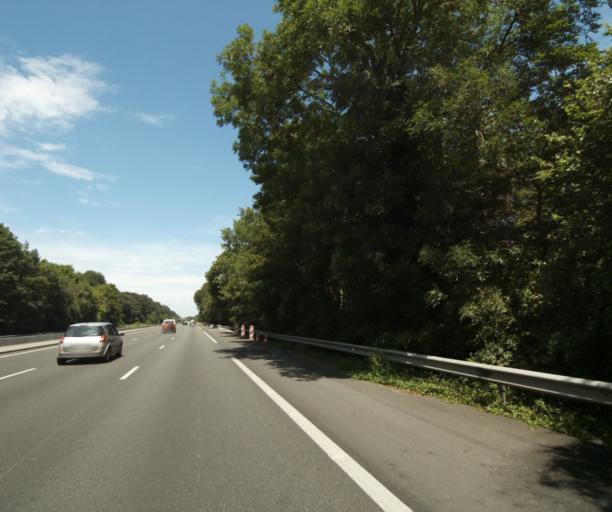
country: FR
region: Ile-de-France
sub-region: Departement de l'Essonne
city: Soisy-sur-Ecole
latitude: 48.4910
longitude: 2.5130
